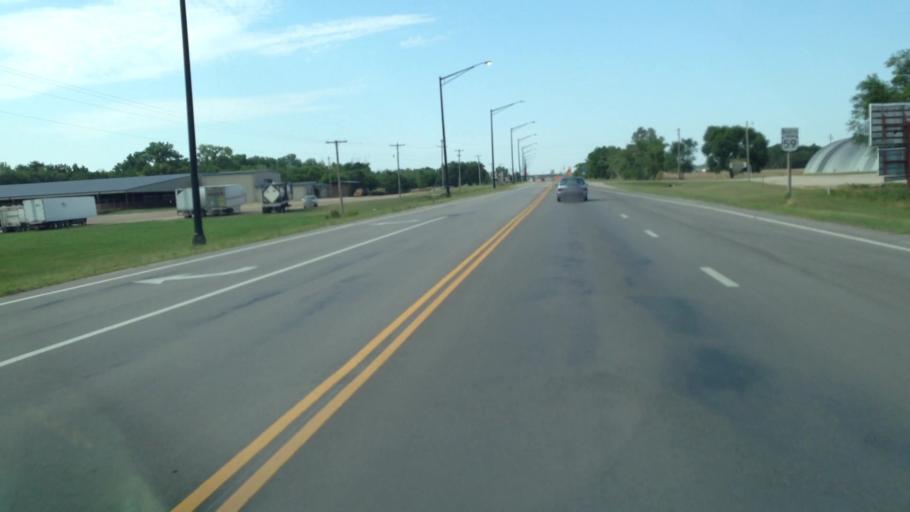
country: US
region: Kansas
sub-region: Labette County
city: Parsons
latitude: 37.3555
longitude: -95.2588
